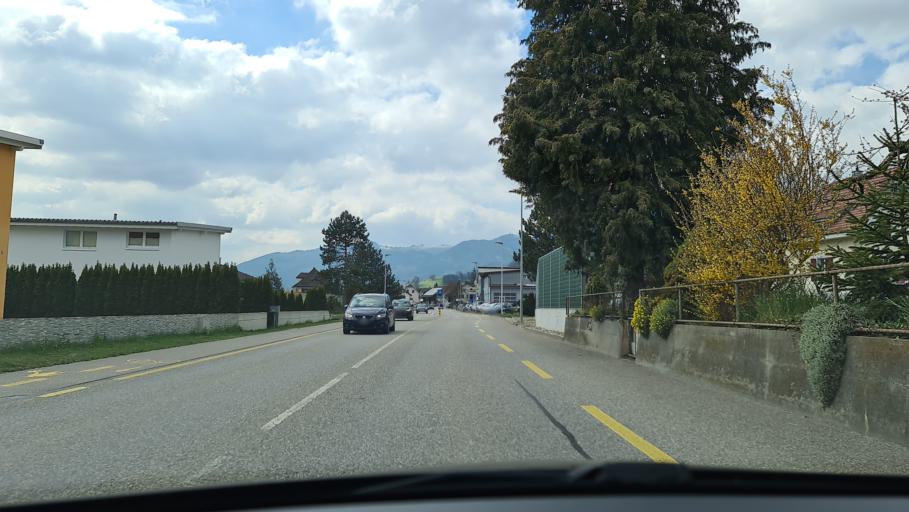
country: CH
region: Solothurn
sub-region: Bezirk Thal
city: Laupersdorf
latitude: 47.3120
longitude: 7.6575
